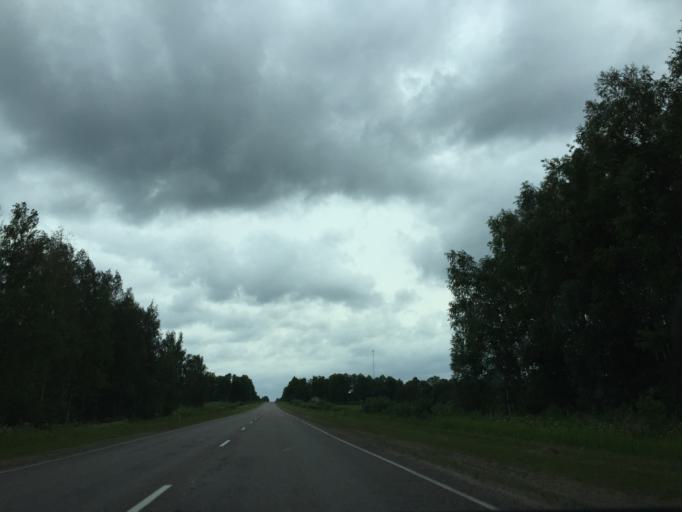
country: LV
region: Smiltene
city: Smiltene
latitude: 57.4014
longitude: 26.0286
